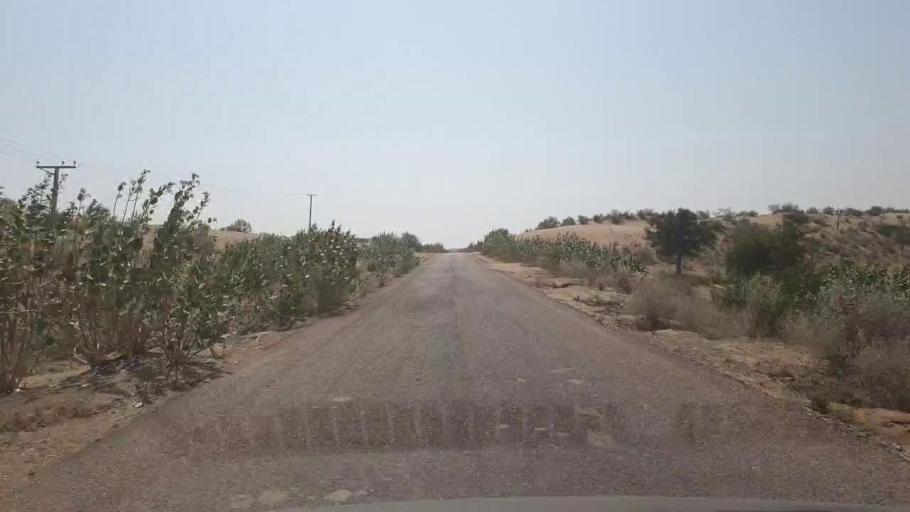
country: PK
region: Sindh
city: Chor
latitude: 25.6583
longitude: 70.1671
